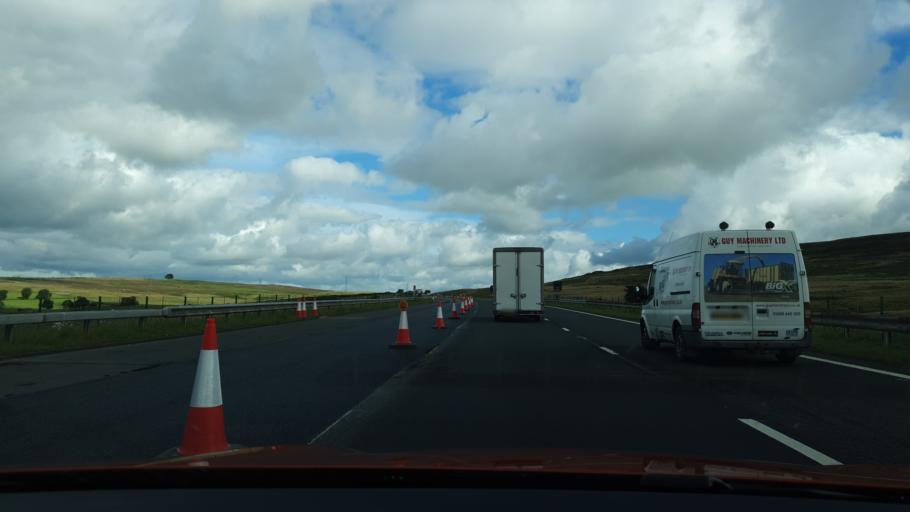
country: GB
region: England
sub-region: Cumbria
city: Appleby-in-Westmorland
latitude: 54.4838
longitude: -2.6371
